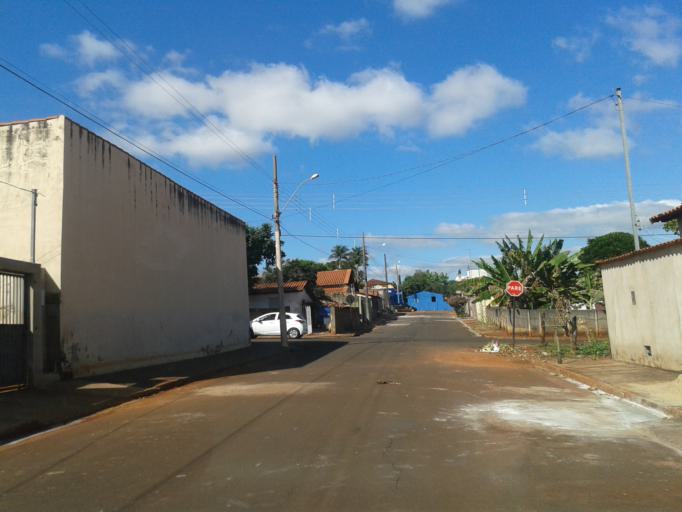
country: BR
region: Minas Gerais
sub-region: Centralina
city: Centralina
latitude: -18.5830
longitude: -49.1957
